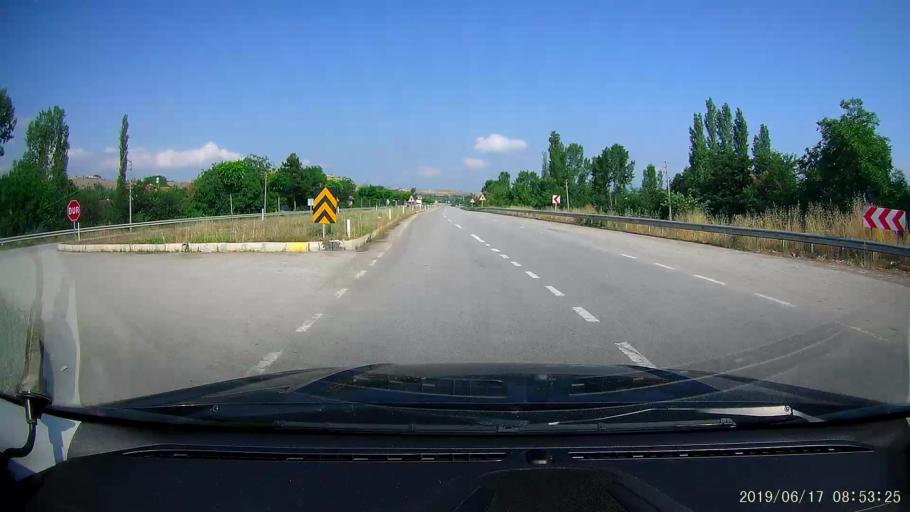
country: TR
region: Tokat
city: Erbaa
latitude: 40.7097
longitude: 36.4818
